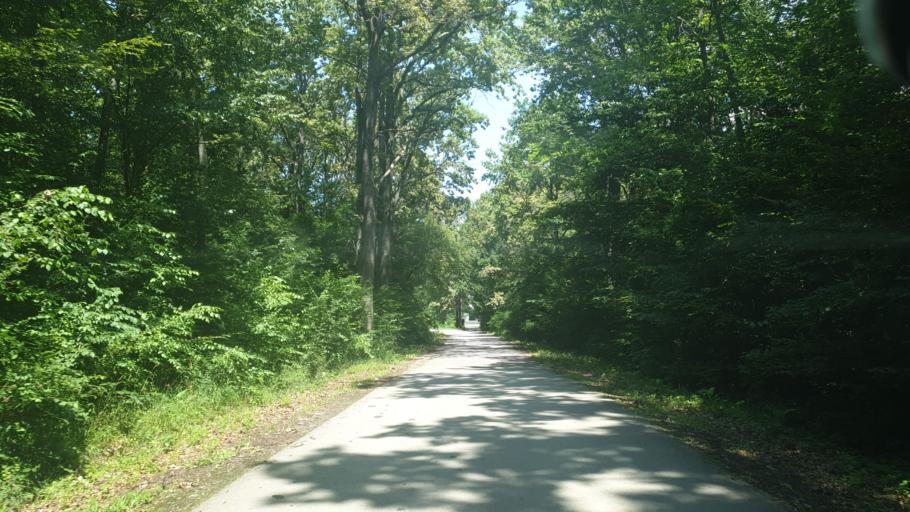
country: RS
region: Autonomna Pokrajina Vojvodina
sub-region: Sremski Okrug
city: Sid
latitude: 45.0415
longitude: 19.1383
